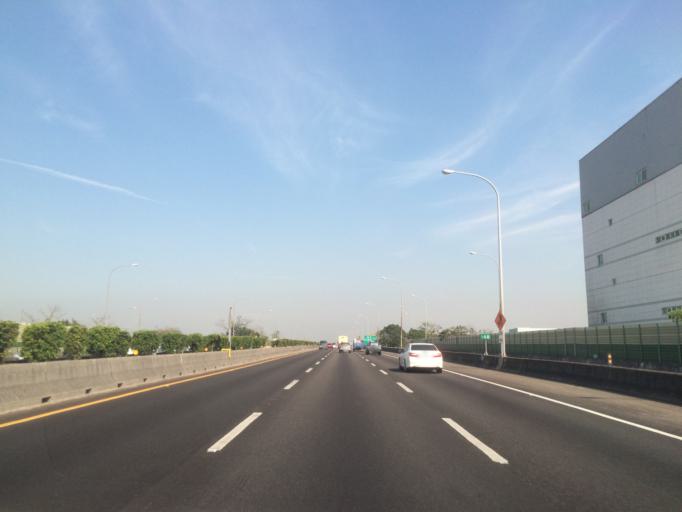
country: TW
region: Taiwan
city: Fengyuan
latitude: 24.2478
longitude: 120.6901
